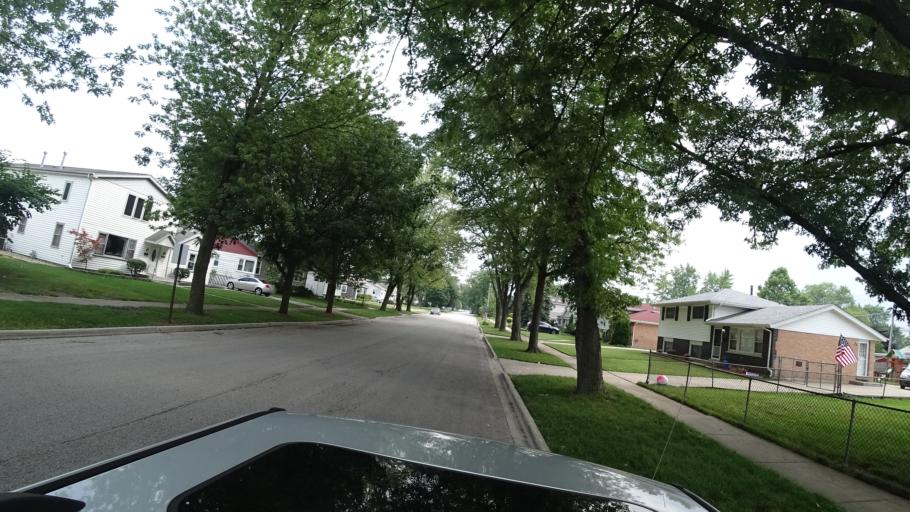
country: US
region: Illinois
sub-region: Cook County
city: Chicago Ridge
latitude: 41.6958
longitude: -87.7754
